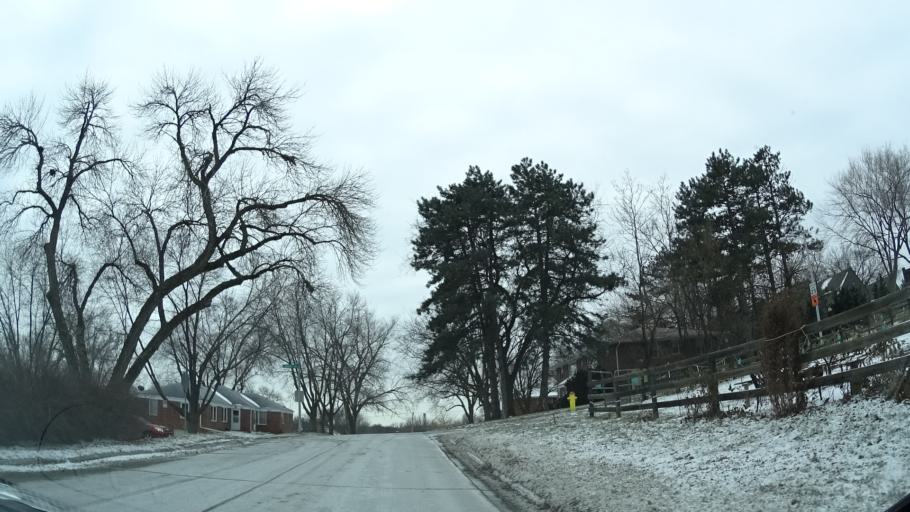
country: US
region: Nebraska
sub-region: Douglas County
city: Omaha
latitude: 41.2717
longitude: -96.0049
